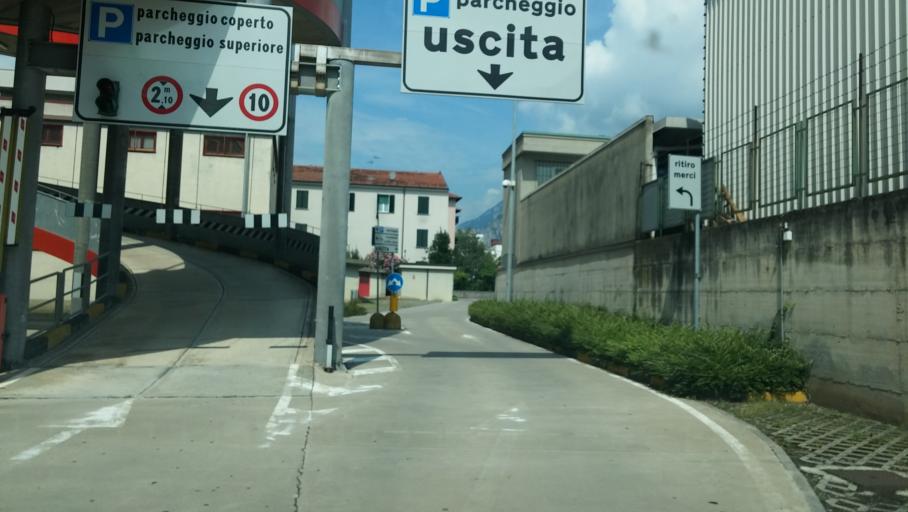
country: IT
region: Lombardy
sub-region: Provincia di Lecco
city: Pescate
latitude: 45.8407
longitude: 9.4024
